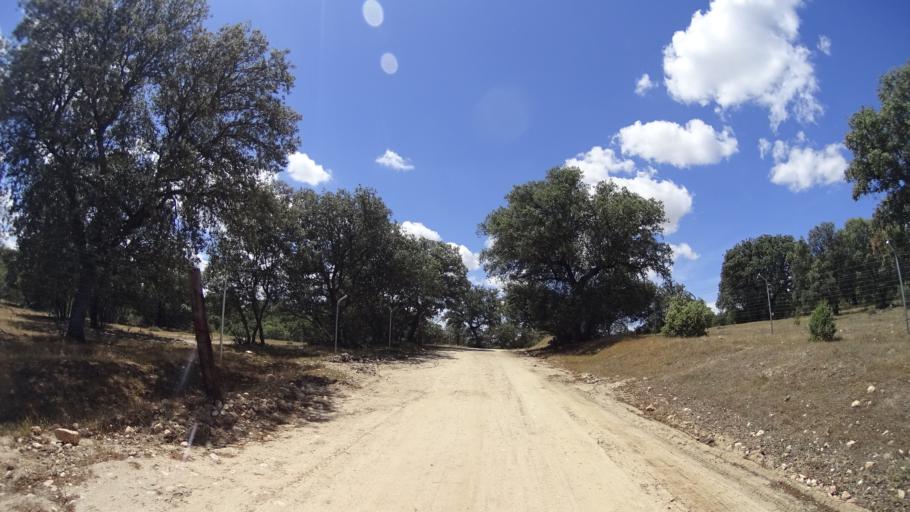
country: ES
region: Madrid
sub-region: Provincia de Madrid
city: Villanueva del Pardillo
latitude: 40.4377
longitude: -3.9570
